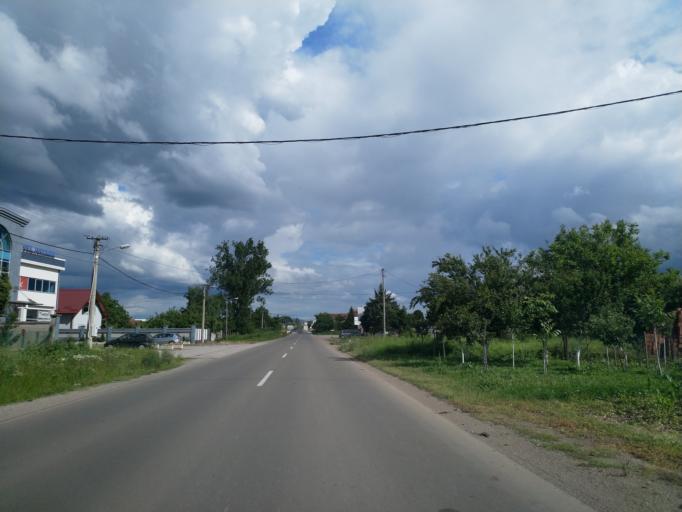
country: RS
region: Central Serbia
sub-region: Pomoravski Okrug
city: Paracin
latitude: 43.8754
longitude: 21.3958
